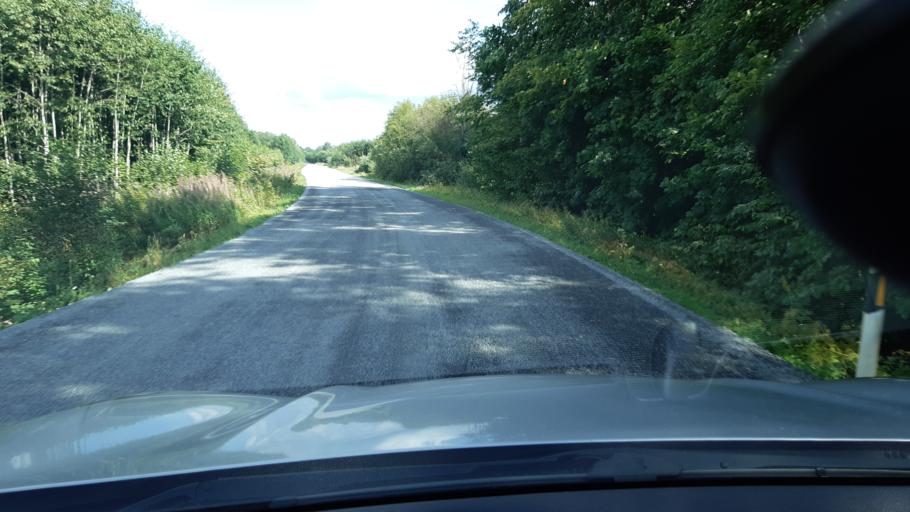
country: EE
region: Raplamaa
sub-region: Kehtna vald
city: Kehtna
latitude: 58.9042
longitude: 25.0957
